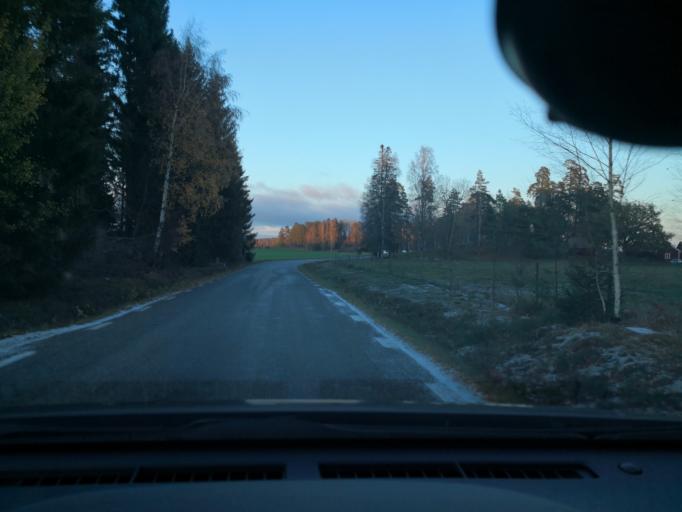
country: SE
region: Vaestmanland
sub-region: Vasteras
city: Tillberga
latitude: 59.7690
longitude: 16.5941
